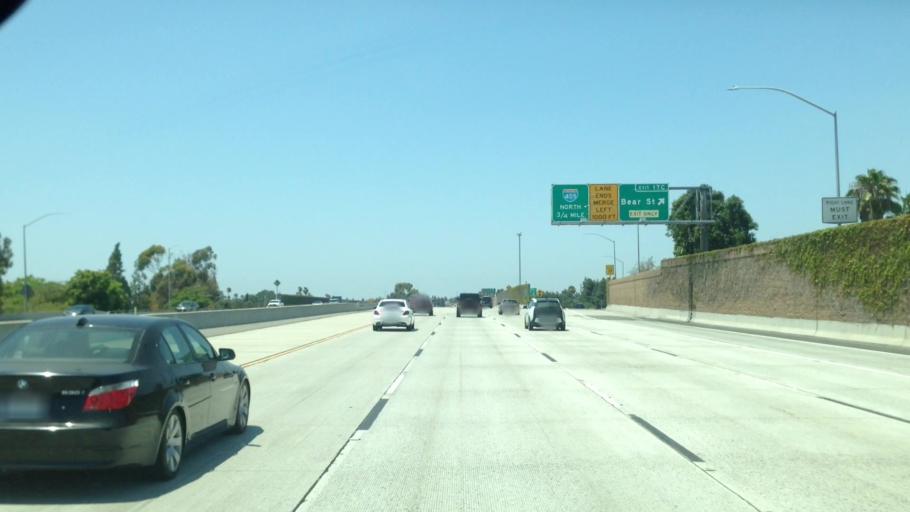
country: US
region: California
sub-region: Orange County
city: Costa Mesa
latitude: 33.6792
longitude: -117.8910
